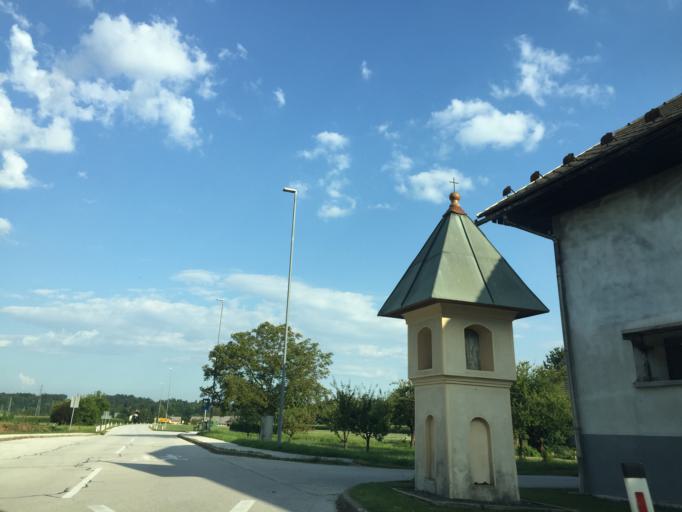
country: SI
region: Radovljica
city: Radovljica
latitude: 46.3230
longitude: 14.2233
